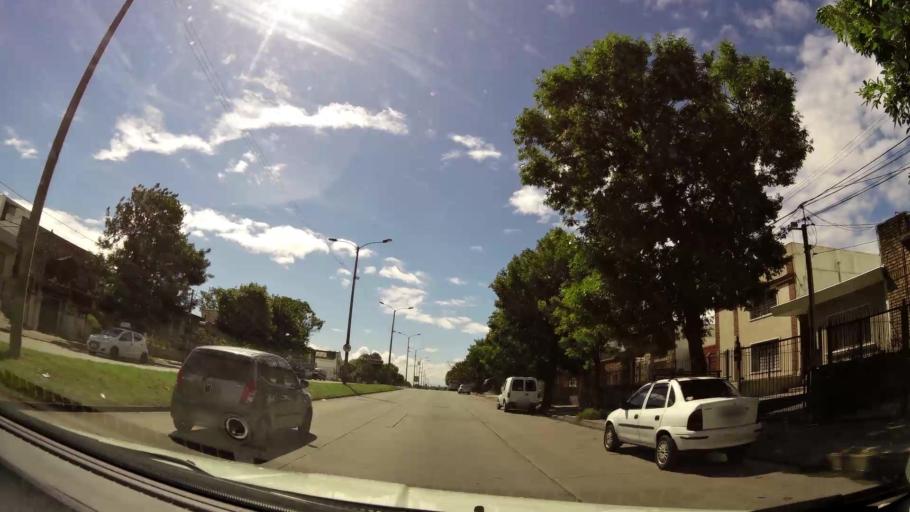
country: UY
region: Montevideo
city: Montevideo
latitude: -34.8549
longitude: -56.1796
